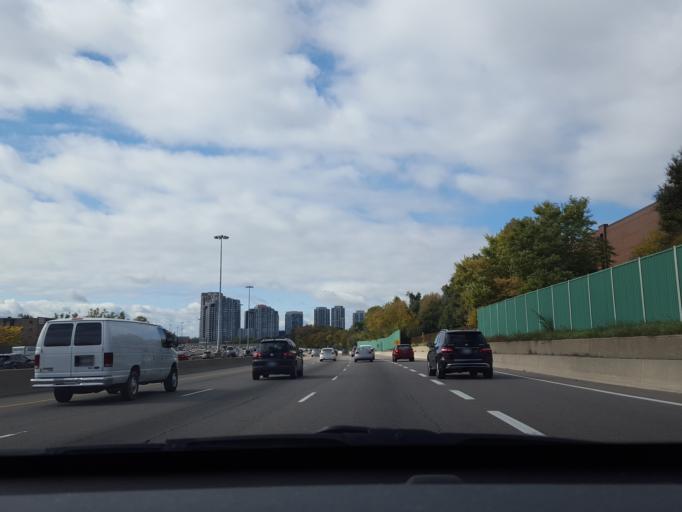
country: CA
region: Ontario
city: Willowdale
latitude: 43.7625
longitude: -79.3919
